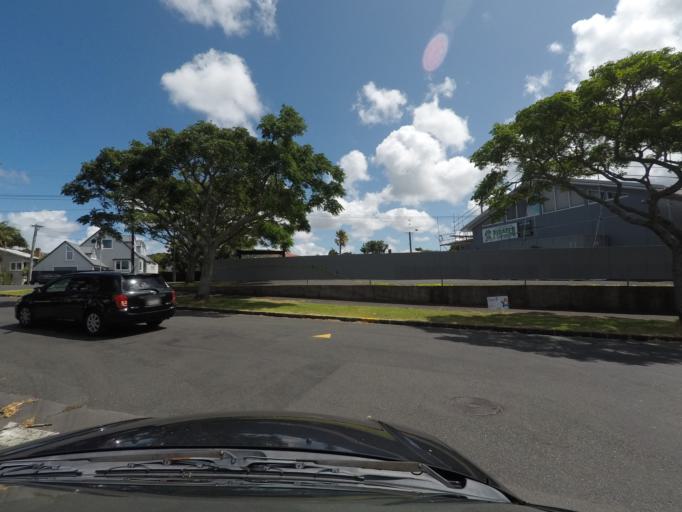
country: NZ
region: Auckland
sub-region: Auckland
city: Rosebank
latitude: -36.8568
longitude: 174.7038
